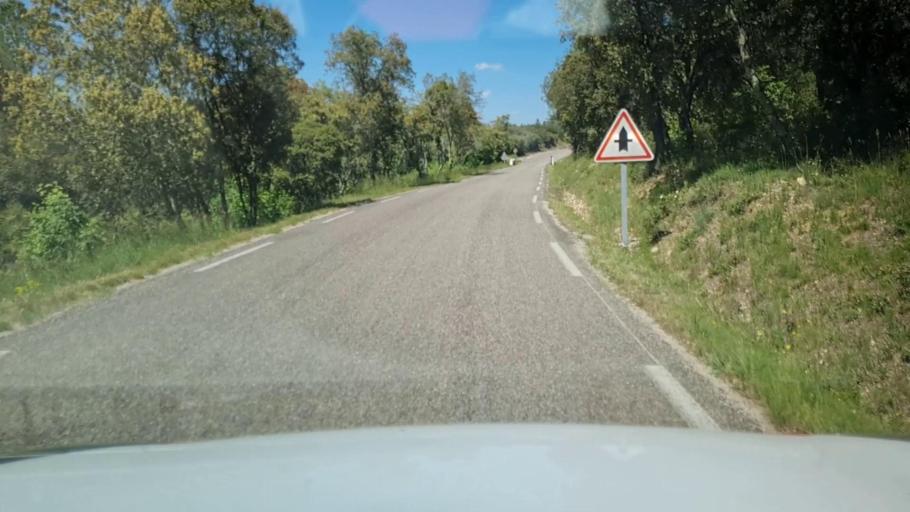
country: FR
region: Languedoc-Roussillon
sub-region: Departement du Gard
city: Clarensac
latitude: 43.8572
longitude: 4.2148
